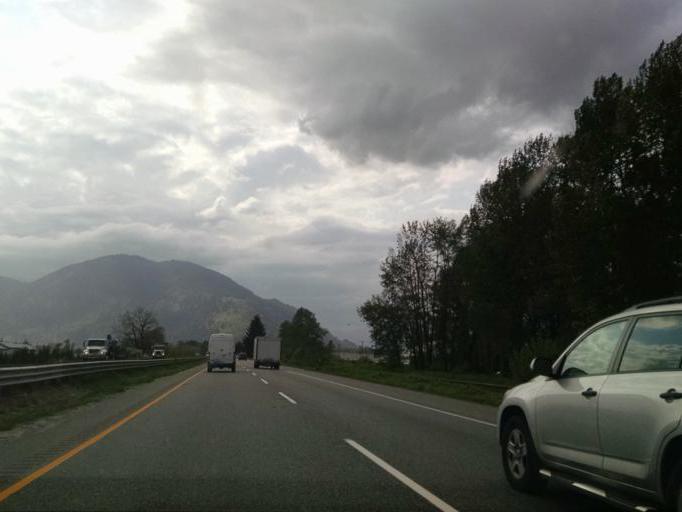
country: CA
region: British Columbia
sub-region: Fraser Valley Regional District
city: Chilliwack
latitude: 49.1408
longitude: -122.0414
